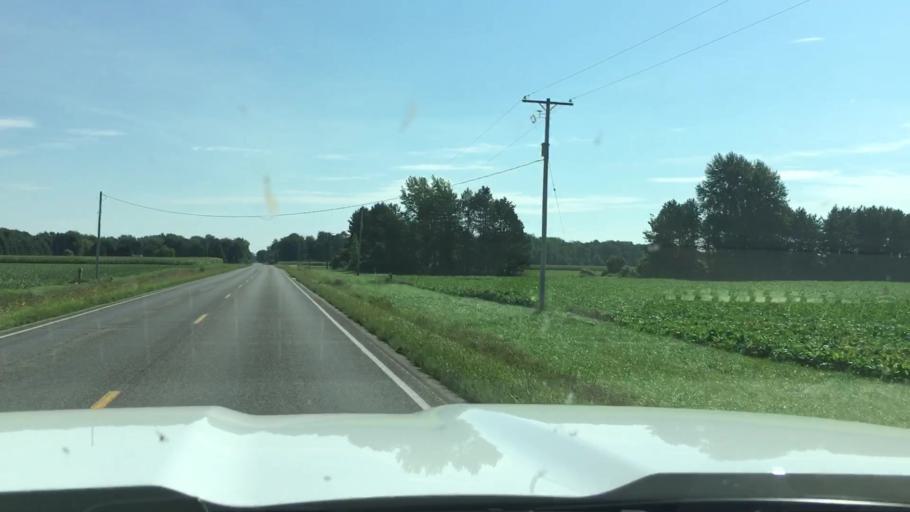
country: US
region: Michigan
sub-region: Saginaw County
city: Freeland
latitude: 43.5244
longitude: -84.1743
